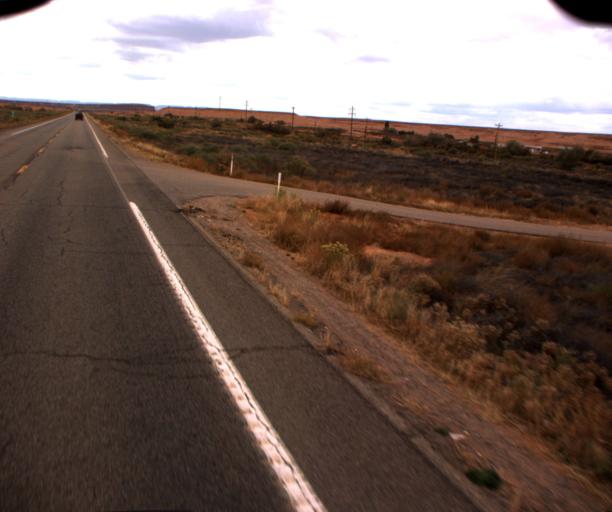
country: US
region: Arizona
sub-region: Navajo County
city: Kayenta
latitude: 36.8308
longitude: -109.8583
